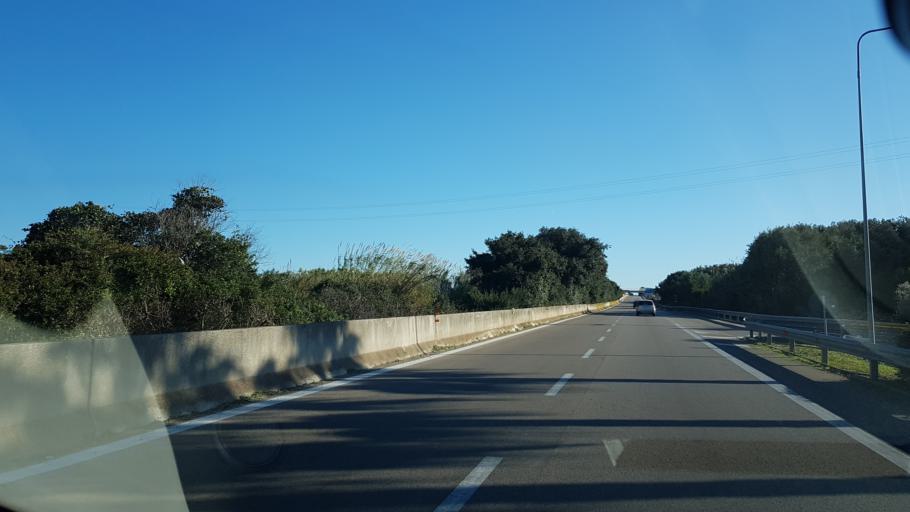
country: IT
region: Apulia
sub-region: Provincia di Lecce
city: Alezio
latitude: 40.0178
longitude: 18.0448
